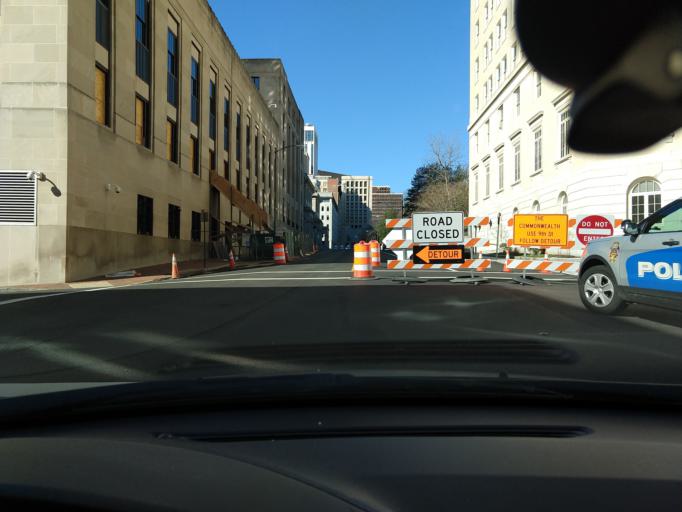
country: US
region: Virginia
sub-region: City of Richmond
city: Richmond
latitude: 37.5372
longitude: -77.4332
